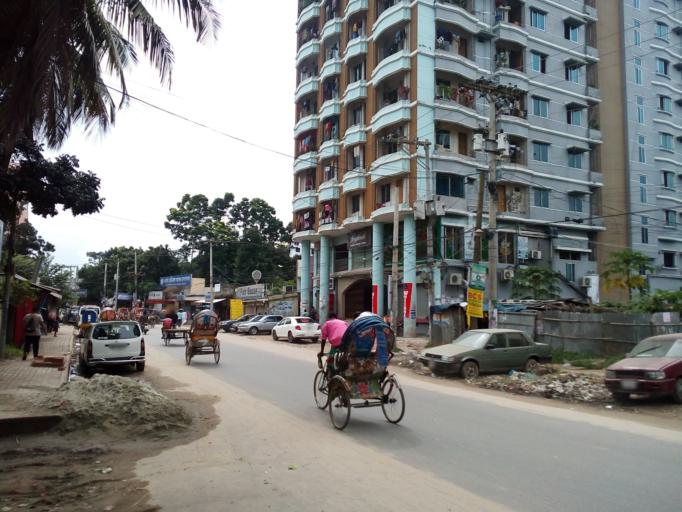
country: BD
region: Dhaka
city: Tungi
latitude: 23.8385
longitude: 90.2521
